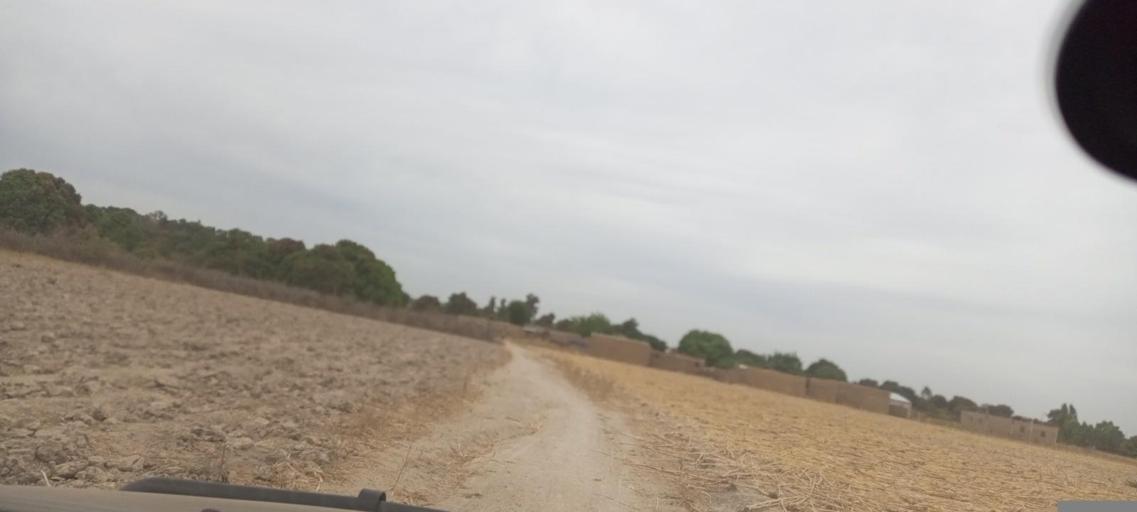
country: ML
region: Koulikoro
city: Kati
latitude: 12.7410
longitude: -8.3293
